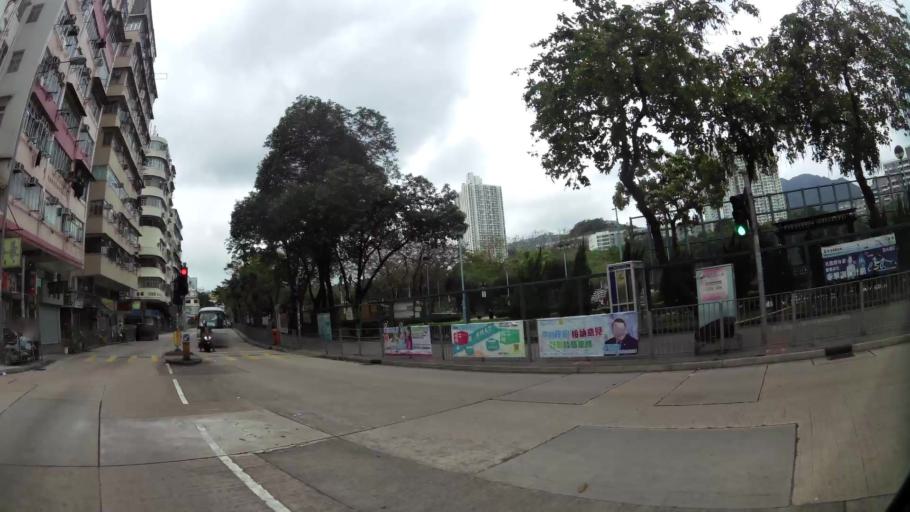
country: HK
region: Kowloon City
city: Kowloon
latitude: 22.3305
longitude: 114.1915
